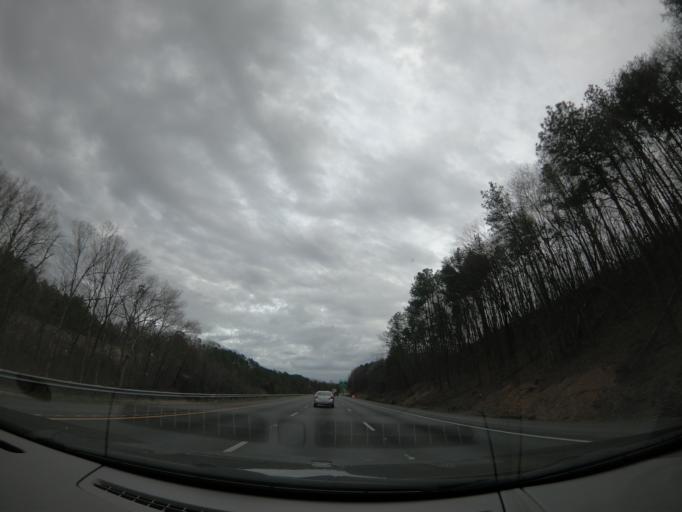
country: US
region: Georgia
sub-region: Catoosa County
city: Indian Springs
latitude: 34.9378
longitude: -85.1617
